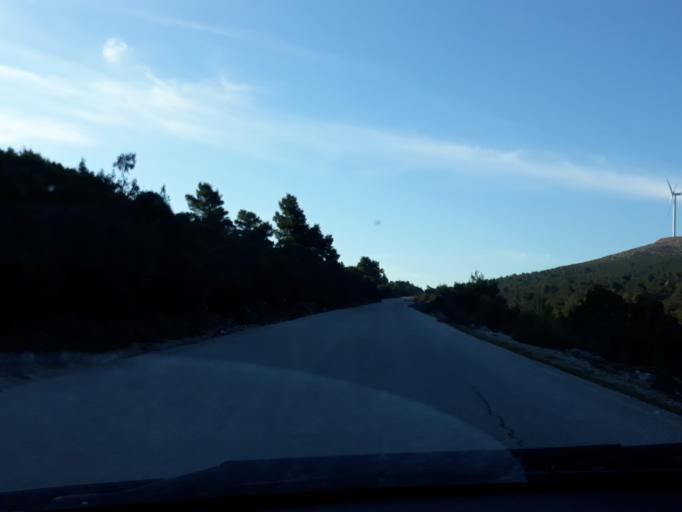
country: GR
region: Attica
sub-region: Nomarchia Dytikis Attikis
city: Fyli
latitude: 38.1593
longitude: 23.6251
